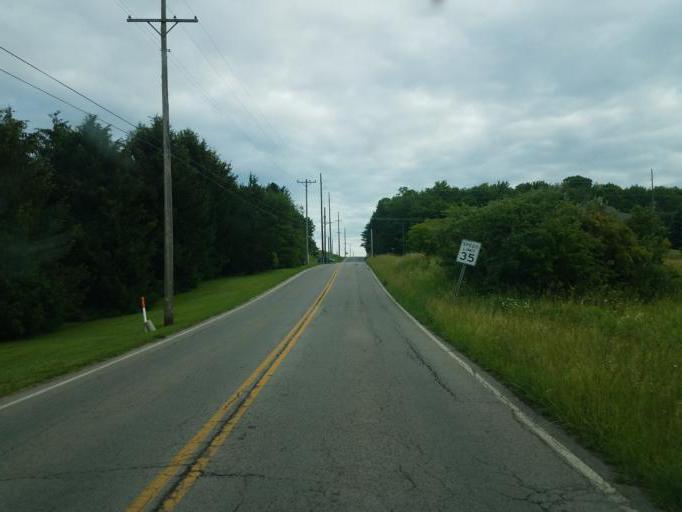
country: US
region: Ohio
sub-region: Richland County
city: Ontario
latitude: 40.7455
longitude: -82.5710
